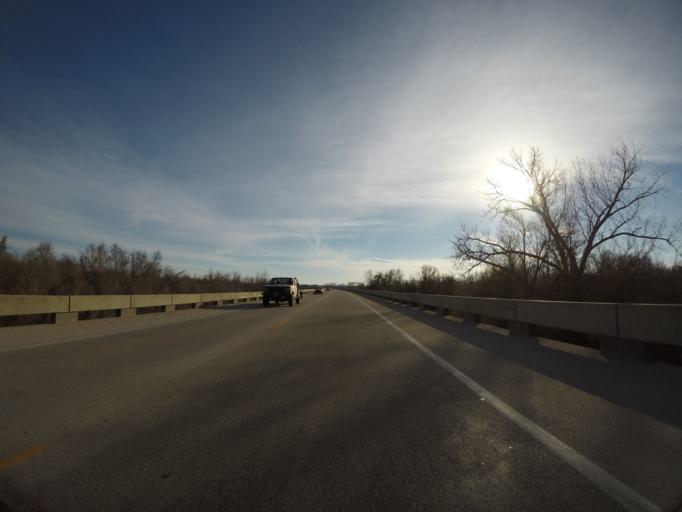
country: US
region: Kansas
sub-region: Shawnee County
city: Topeka
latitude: 39.0837
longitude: -95.6132
